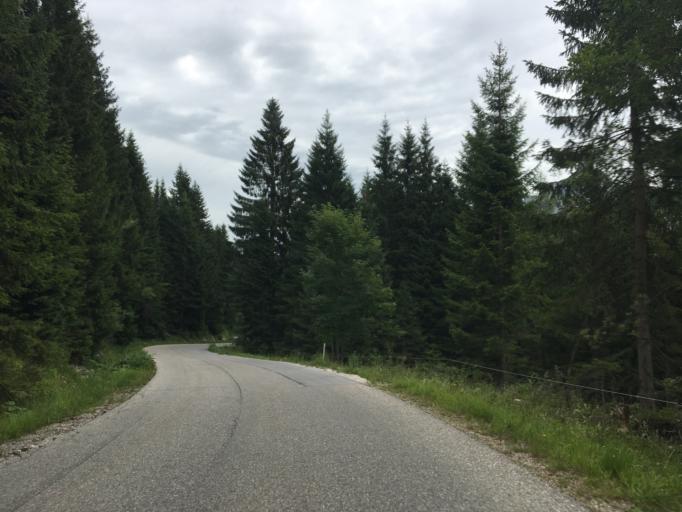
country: AT
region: Salzburg
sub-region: Politischer Bezirk Salzburg-Umgebung
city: Strobl
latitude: 47.6584
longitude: 13.4411
